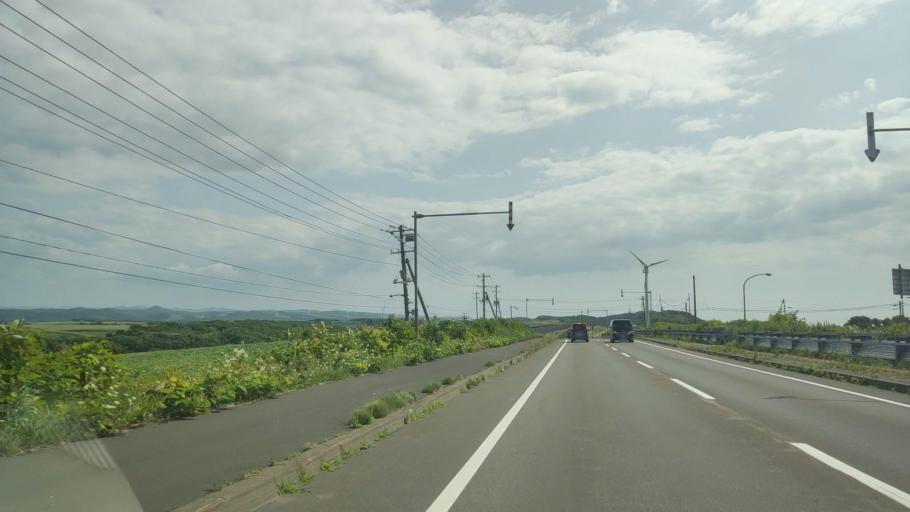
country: JP
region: Hokkaido
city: Rumoi
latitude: 44.3017
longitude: 141.6530
